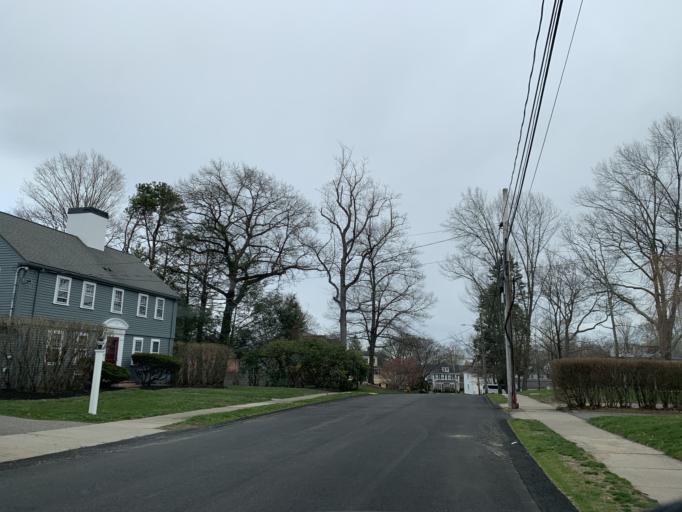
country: US
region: Massachusetts
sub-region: Norfolk County
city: Norwood
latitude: 42.1906
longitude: -71.2082
